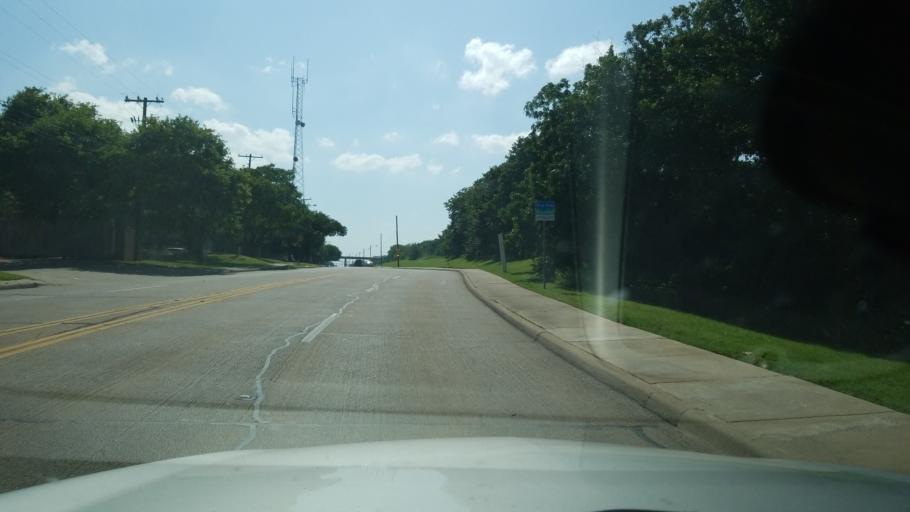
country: US
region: Texas
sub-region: Dallas County
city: Irving
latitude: 32.8148
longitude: -96.9532
